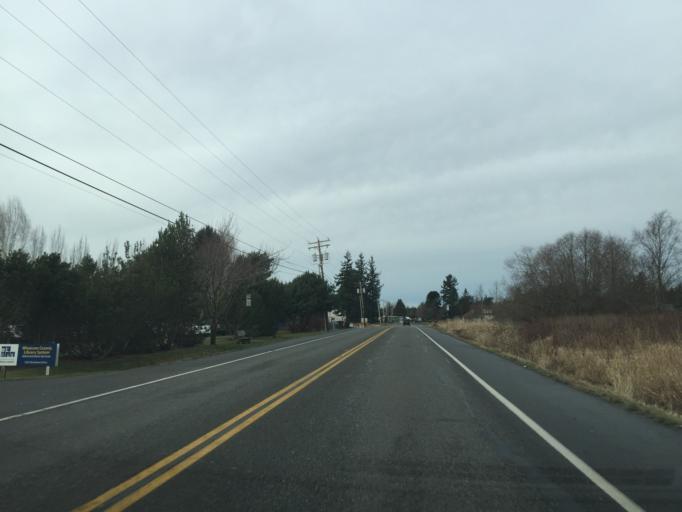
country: US
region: Washington
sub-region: Whatcom County
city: Marietta-Alderwood
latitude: 48.8296
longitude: -122.5380
